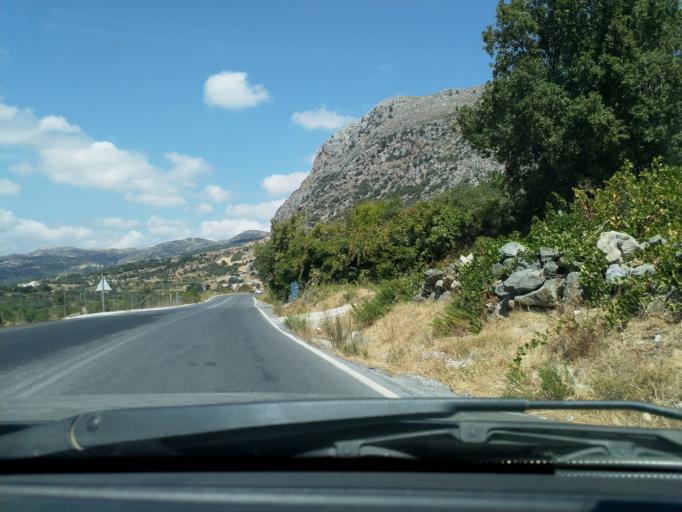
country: GR
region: Crete
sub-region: Nomos Rethymnis
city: Agia Foteini
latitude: 35.1990
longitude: 24.5439
